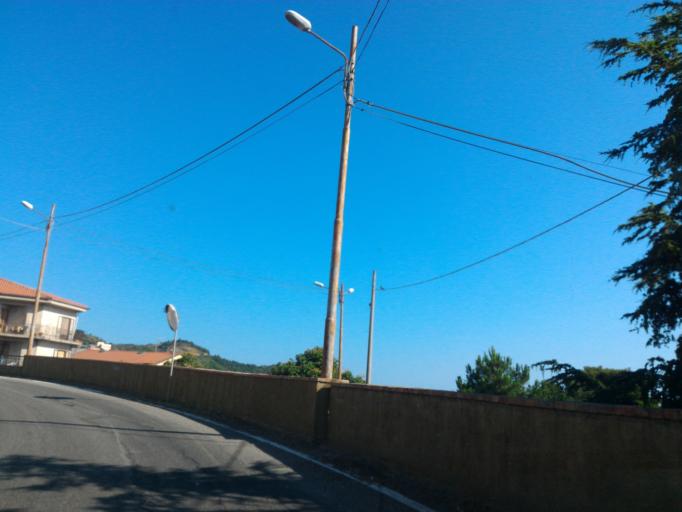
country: IT
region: Calabria
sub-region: Provincia di Crotone
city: Ciro
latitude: 39.3819
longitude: 17.0668
